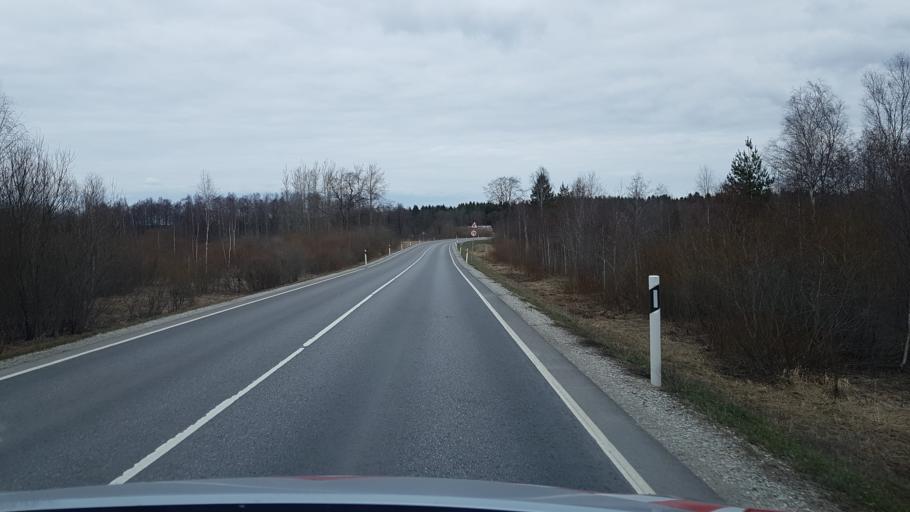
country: EE
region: Ida-Virumaa
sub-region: Narva-Joesuu linn
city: Narva-Joesuu
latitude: 59.4091
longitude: 28.0678
